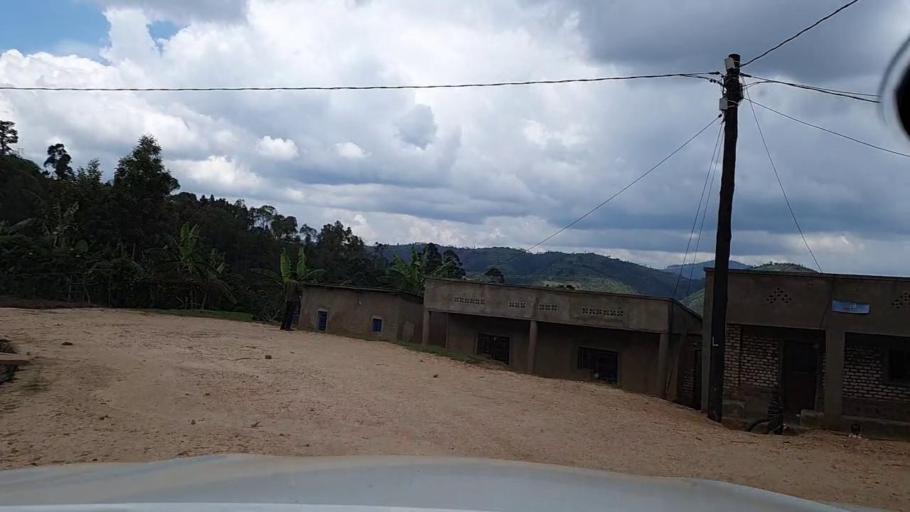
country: RW
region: Southern Province
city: Nzega
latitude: -2.6365
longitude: 29.4901
